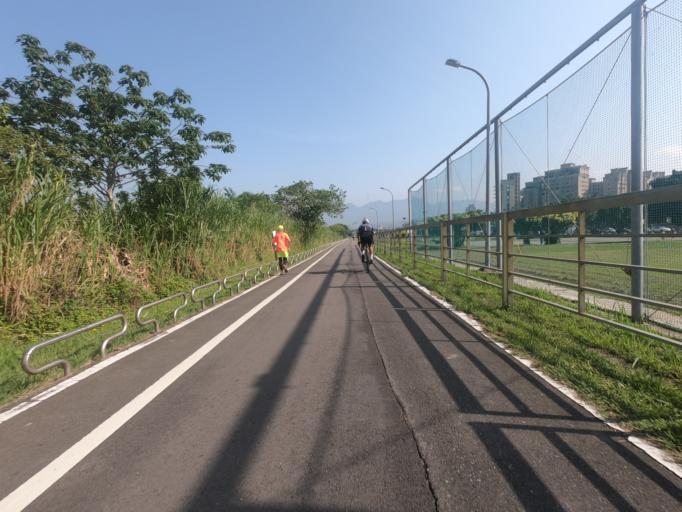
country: TW
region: Taipei
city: Taipei
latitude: 25.0854
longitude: 121.5148
